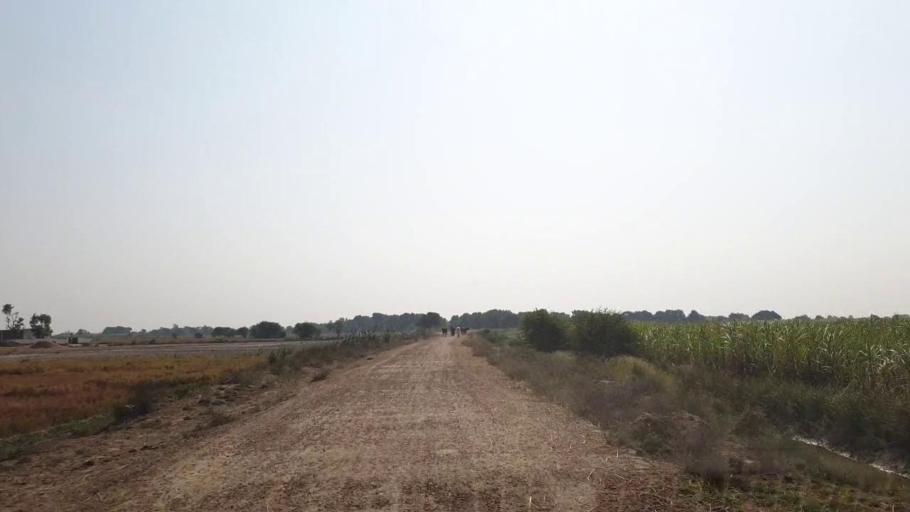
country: PK
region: Sindh
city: Tando Muhammad Khan
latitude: 25.0198
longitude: 68.4171
